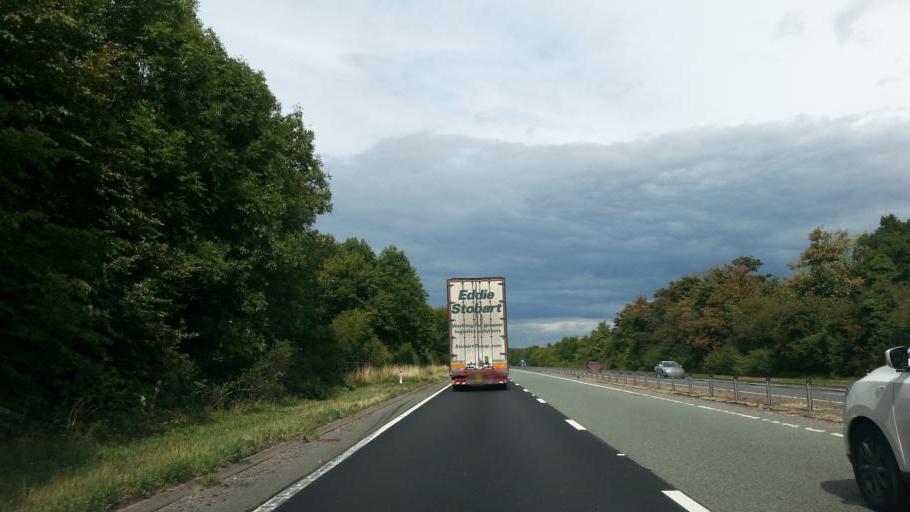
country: GB
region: England
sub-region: Cambridgeshire
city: Sawston
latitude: 52.1042
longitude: 0.2094
